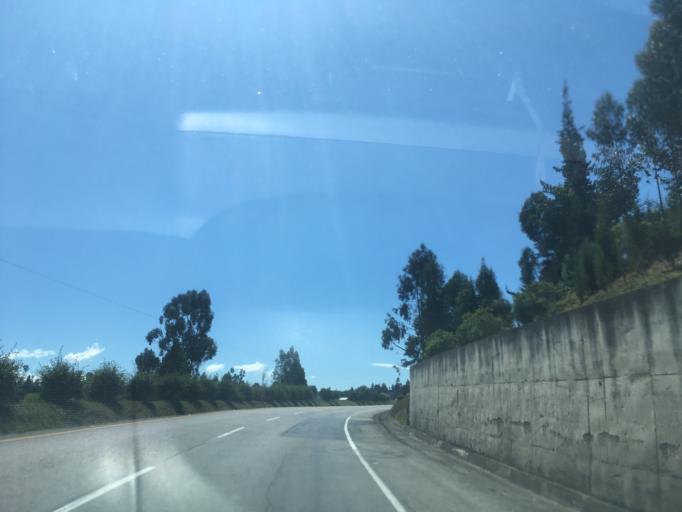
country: CO
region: Boyaca
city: Tuta
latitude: 5.7051
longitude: -73.2453
